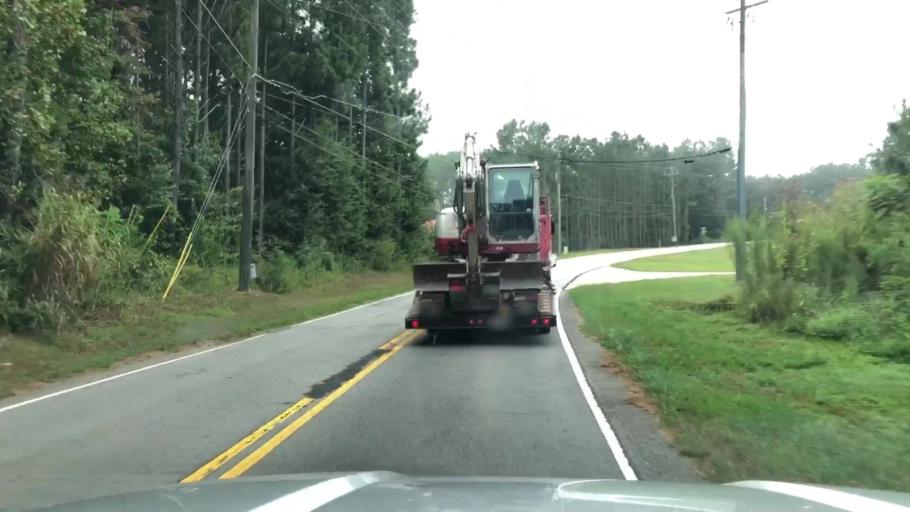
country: US
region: Georgia
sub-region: Bartow County
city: Emerson
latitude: 34.0516
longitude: -84.7797
